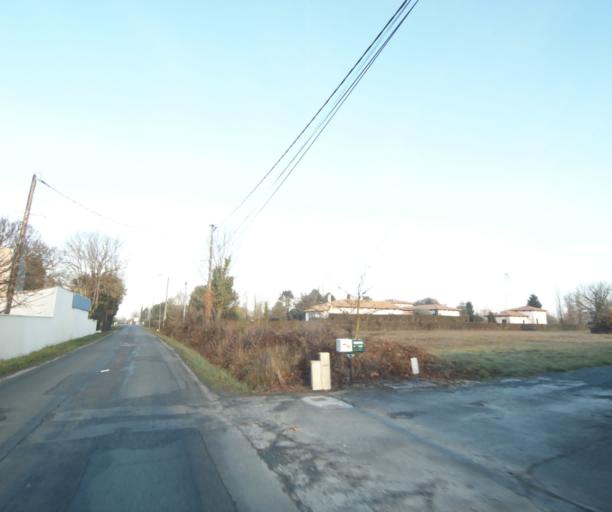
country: FR
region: Poitou-Charentes
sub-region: Departement de la Charente-Maritime
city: Fontcouverte
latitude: 45.7630
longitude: -0.5794
